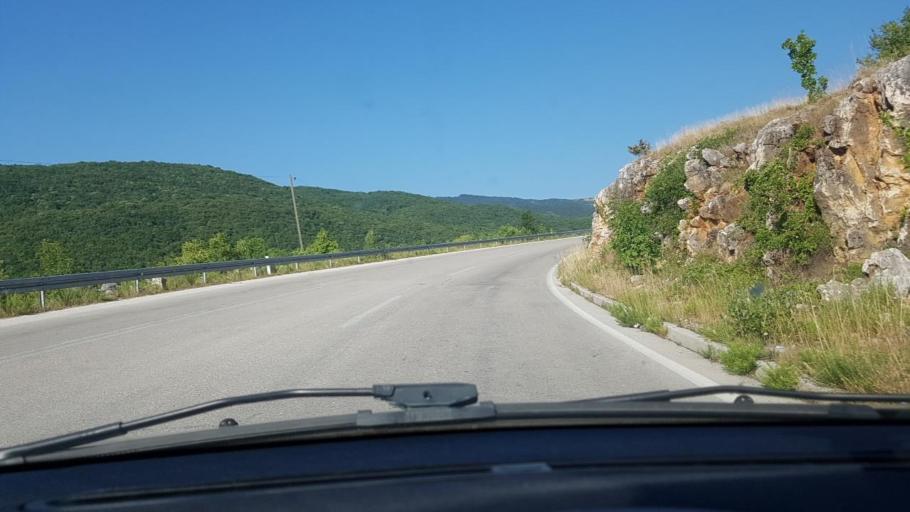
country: BA
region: Federation of Bosnia and Herzegovina
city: Rumboci
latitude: 43.8185
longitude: 17.4658
